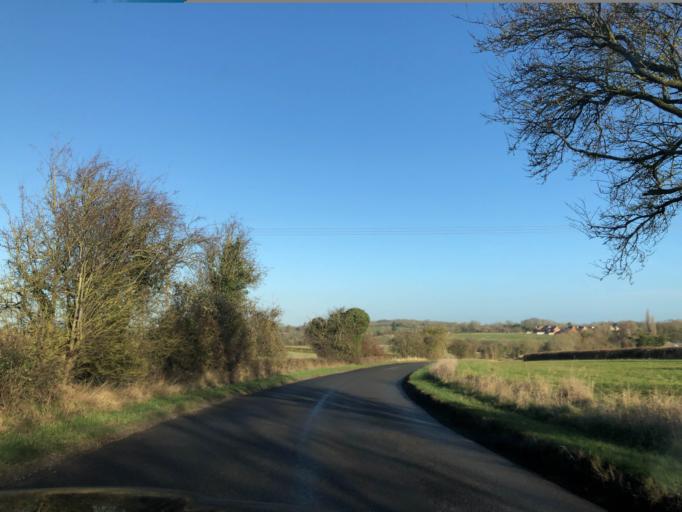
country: GB
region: England
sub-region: Warwickshire
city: Wellesbourne Mountford
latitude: 52.1928
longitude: -1.5142
